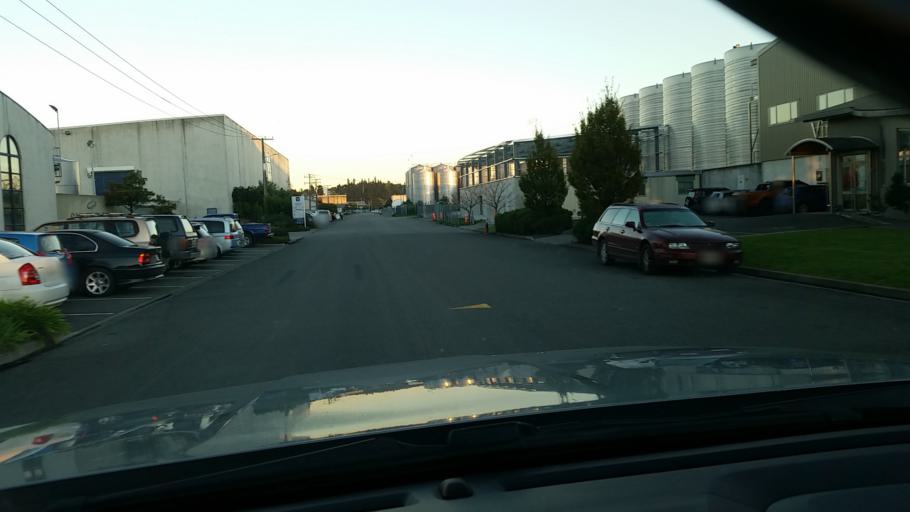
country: NZ
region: Marlborough
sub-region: Marlborough District
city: Blenheim
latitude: -41.5331
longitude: 174.0126
